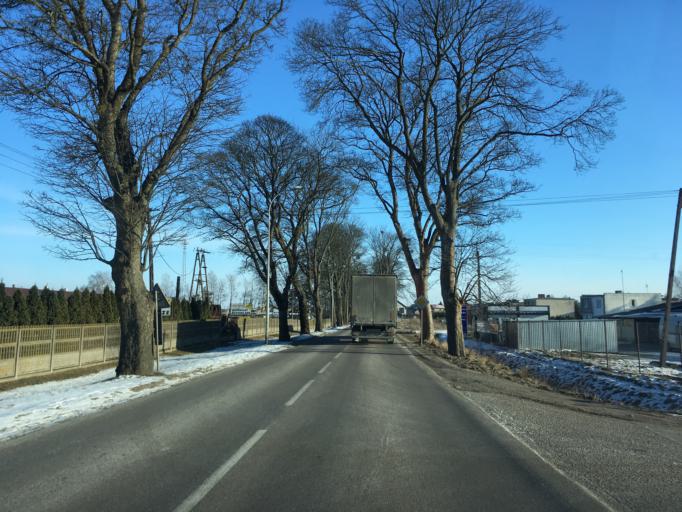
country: PL
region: Pomeranian Voivodeship
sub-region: Powiat starogardzki
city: Zblewo
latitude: 53.9445
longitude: 18.3135
